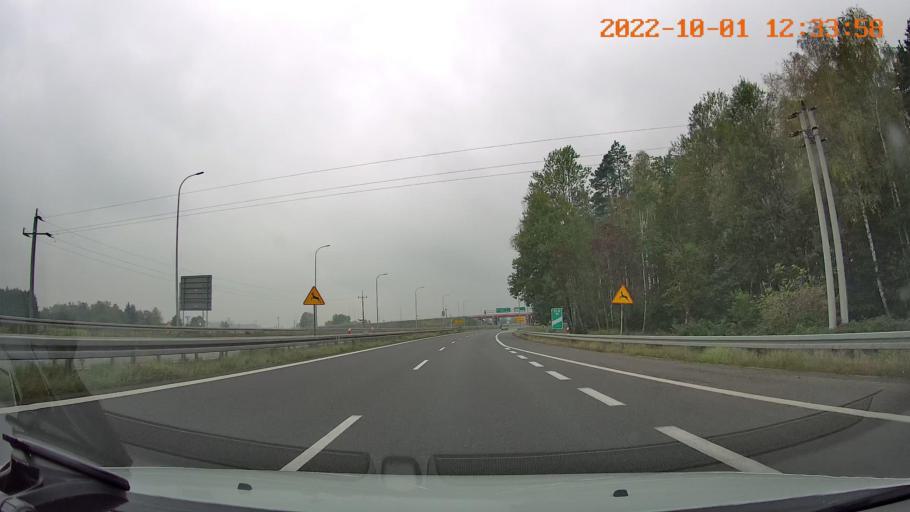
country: PL
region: Silesian Voivodeship
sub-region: Powiat bierunsko-ledzinski
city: Ledziny
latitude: 50.1439
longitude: 19.1020
